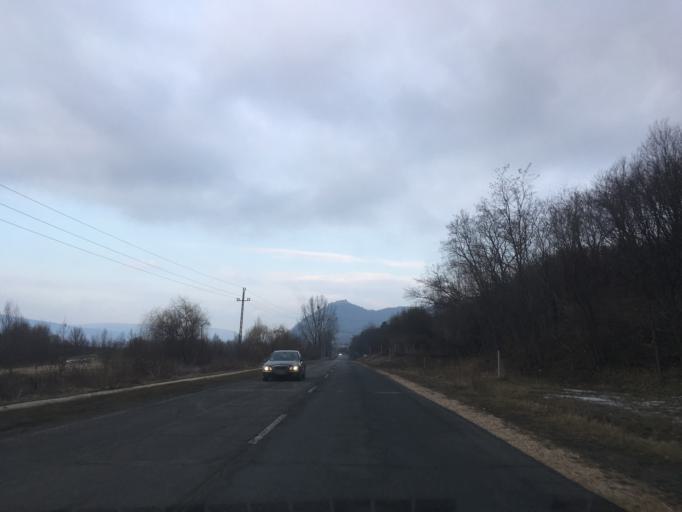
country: HU
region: Pest
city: Visegrad
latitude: 47.7717
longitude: 18.9623
